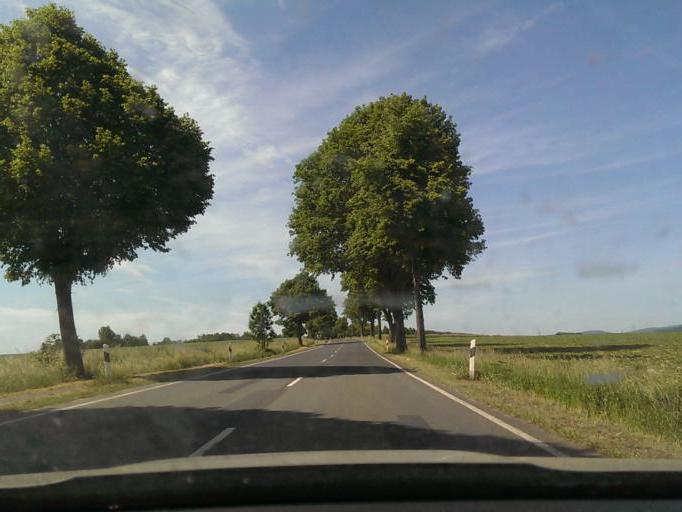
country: DE
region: Lower Saxony
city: Elze
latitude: 52.1422
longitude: 9.7597
